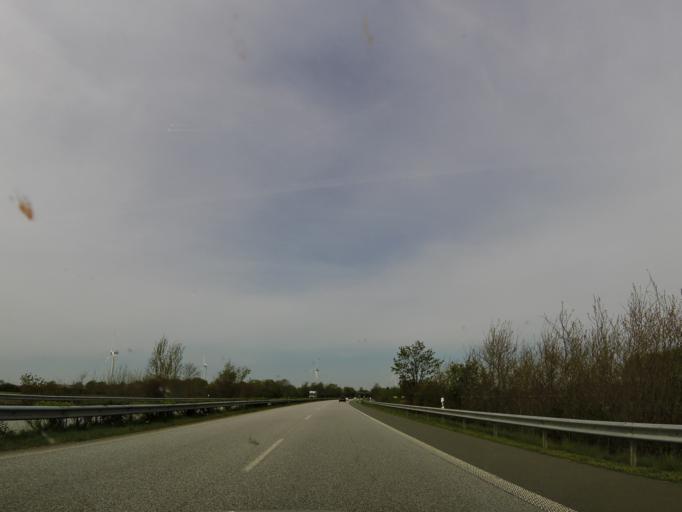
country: DE
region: Schleswig-Holstein
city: Hemmingstedt
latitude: 54.1728
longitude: 9.0687
